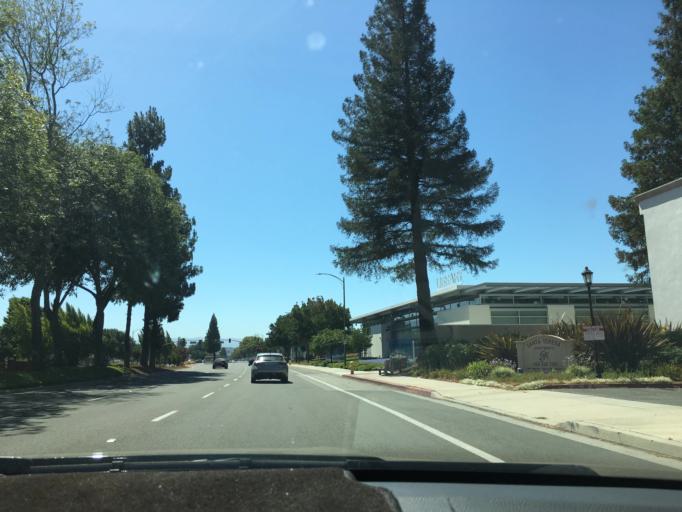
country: US
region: California
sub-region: Santa Clara County
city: Seven Trees
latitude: 37.2371
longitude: -121.7989
